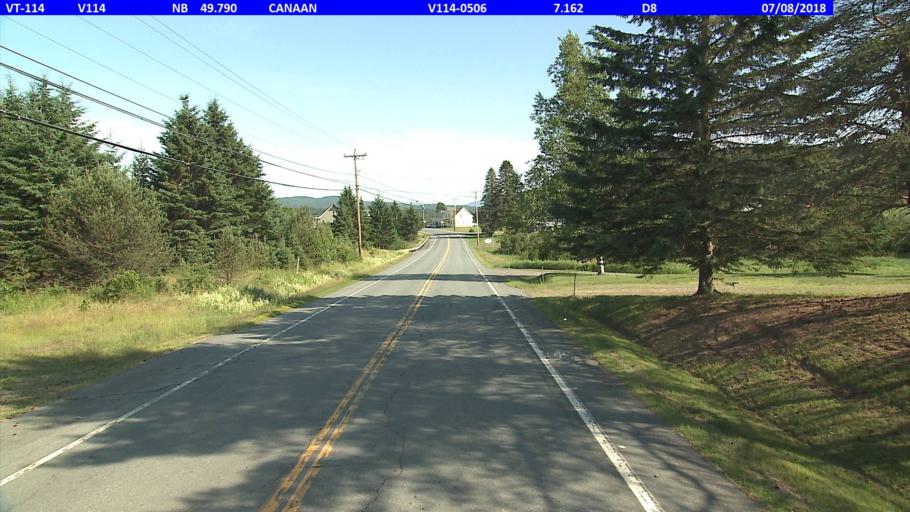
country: US
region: New Hampshire
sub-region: Coos County
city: Colebrook
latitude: 45.0054
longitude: -71.5543
